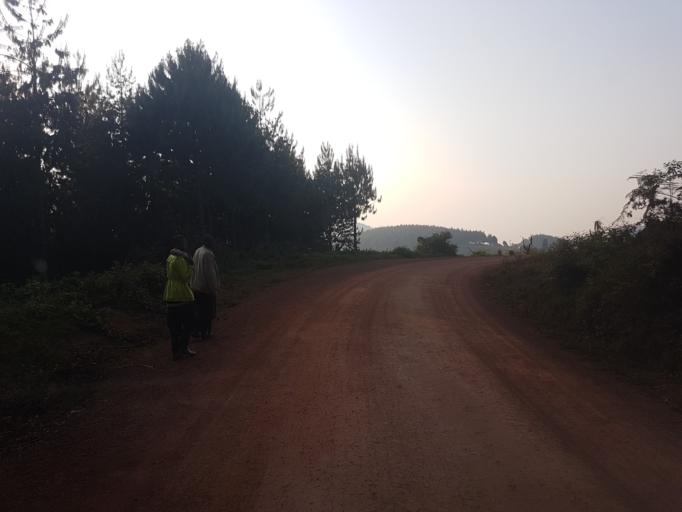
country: UG
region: Western Region
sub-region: Kanungu District
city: Kanungu
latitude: -1.0625
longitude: 29.9039
